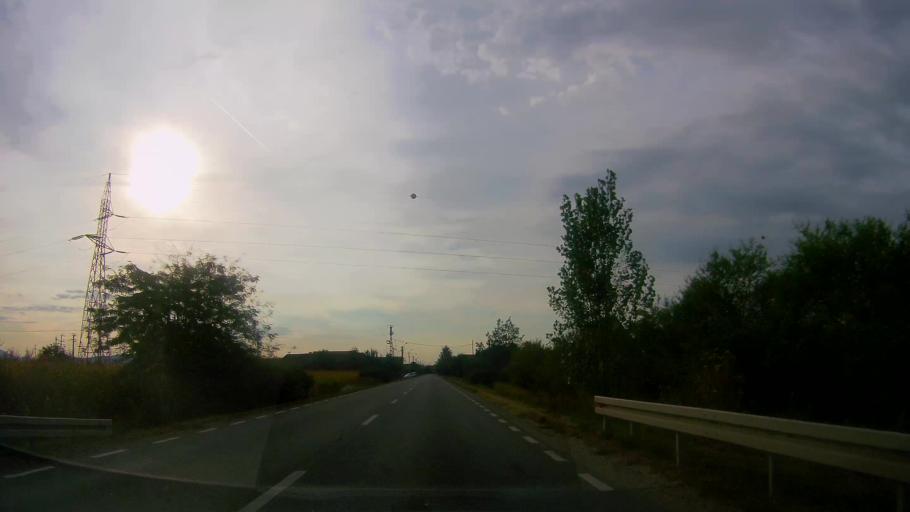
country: RO
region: Satu Mare
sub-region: Comuna Turulung
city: Turulung
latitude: 47.9479
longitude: 23.0705
